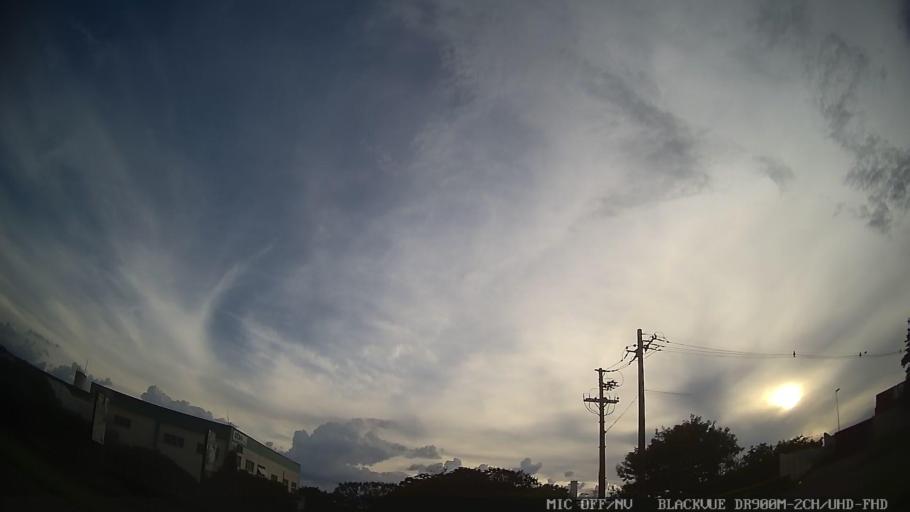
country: BR
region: Sao Paulo
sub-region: Jaguariuna
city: Jaguariuna
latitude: -22.6297
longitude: -47.0447
